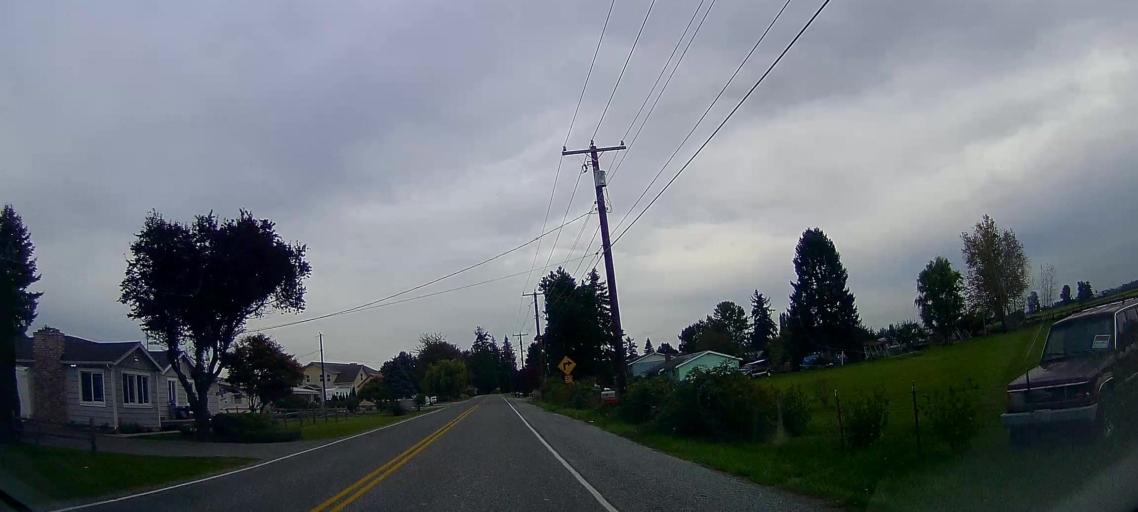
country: US
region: Washington
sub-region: Skagit County
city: Mount Vernon
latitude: 48.4561
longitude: -122.3801
